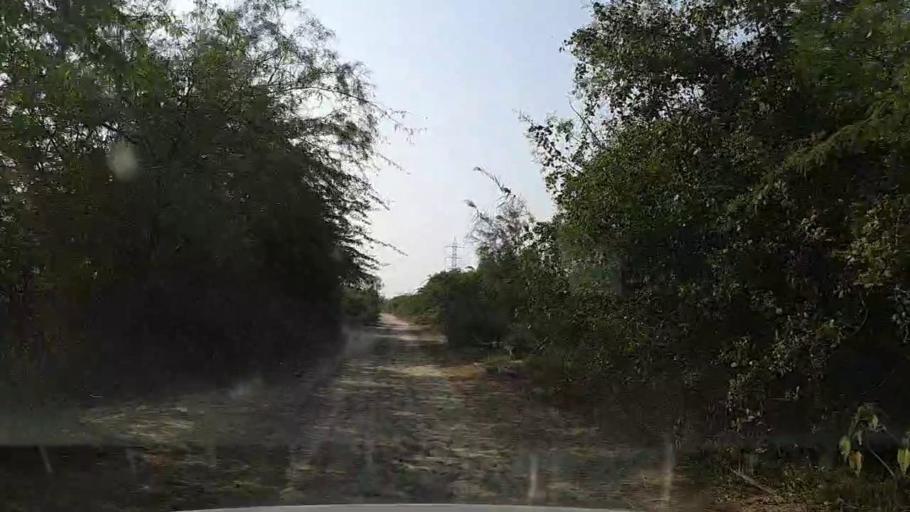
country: PK
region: Sindh
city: Mirpur Sakro
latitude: 24.5754
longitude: 67.5813
